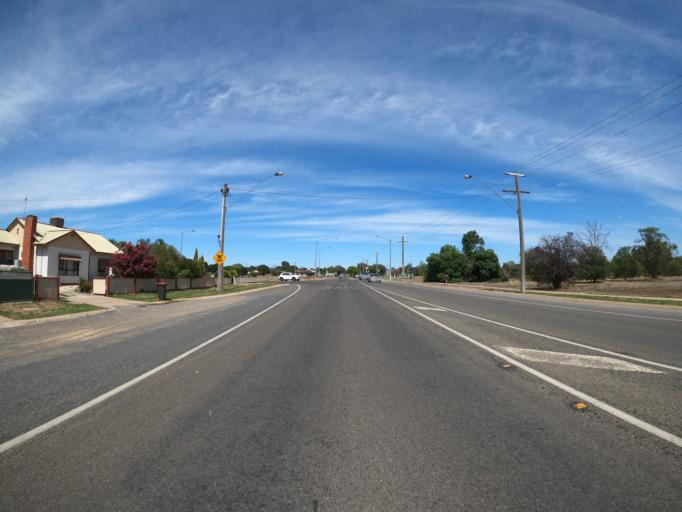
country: AU
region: Victoria
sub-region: Moira
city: Yarrawonga
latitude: -36.0191
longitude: 145.9999
